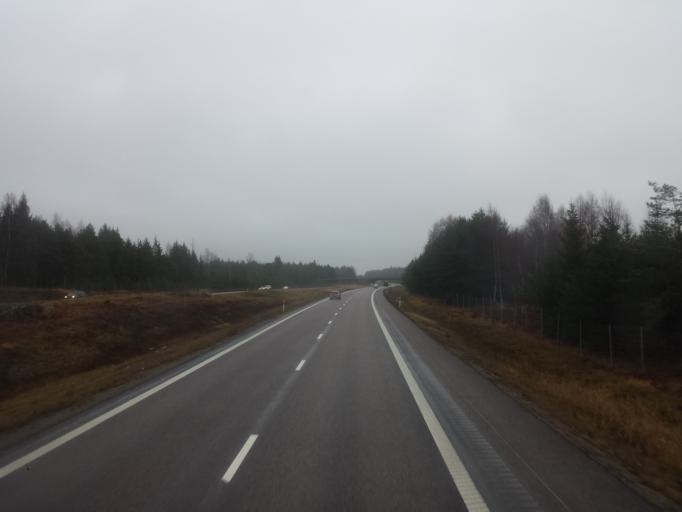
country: SE
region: Soedermanland
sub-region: Nykopings Kommun
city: Stigtomta
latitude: 58.7581
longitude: 16.8067
